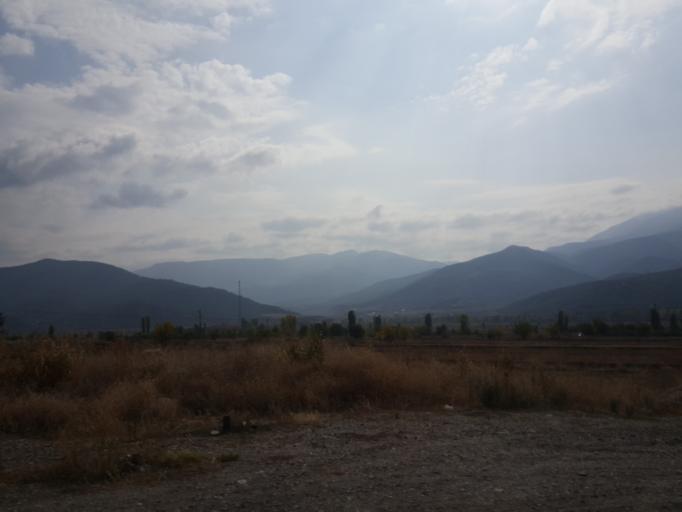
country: TR
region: Corum
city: Hacihamza
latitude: 41.1190
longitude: 34.4073
